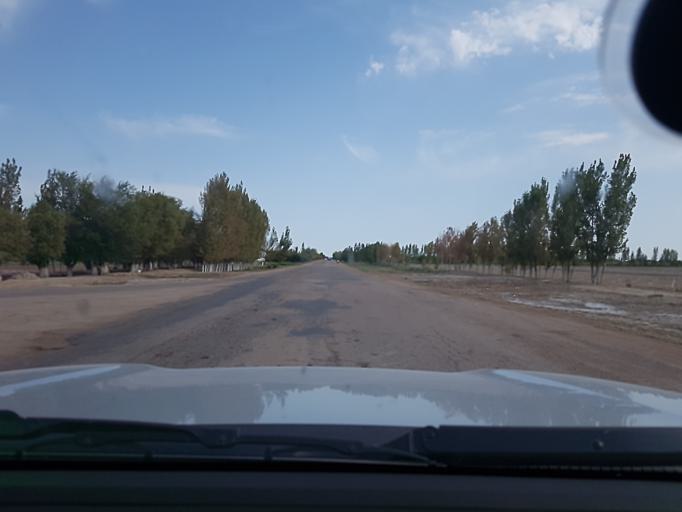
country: TM
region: Dasoguz
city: Boldumsaz
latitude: 42.0292
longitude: 59.8209
